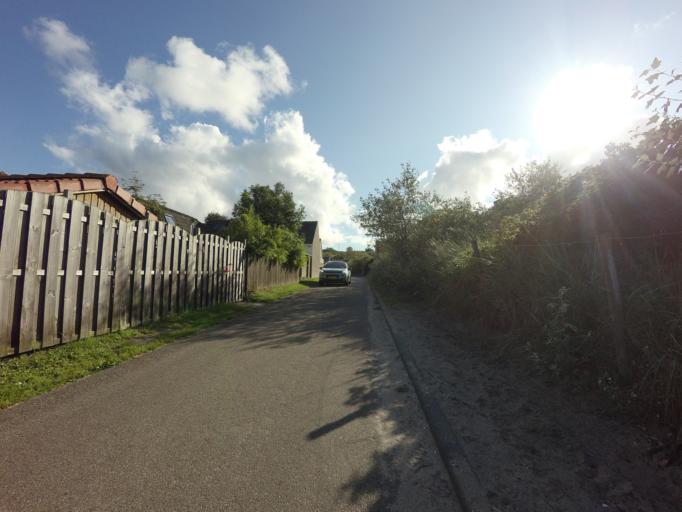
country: NL
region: Friesland
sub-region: Gemeente Terschelling
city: West-Terschelling
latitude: 53.3607
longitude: 5.2127
